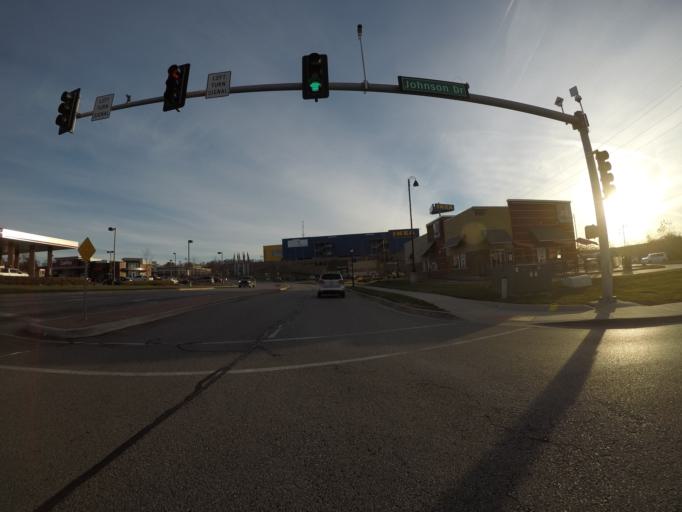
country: US
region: Kansas
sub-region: Johnson County
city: Merriam
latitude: 39.0221
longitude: -94.6906
